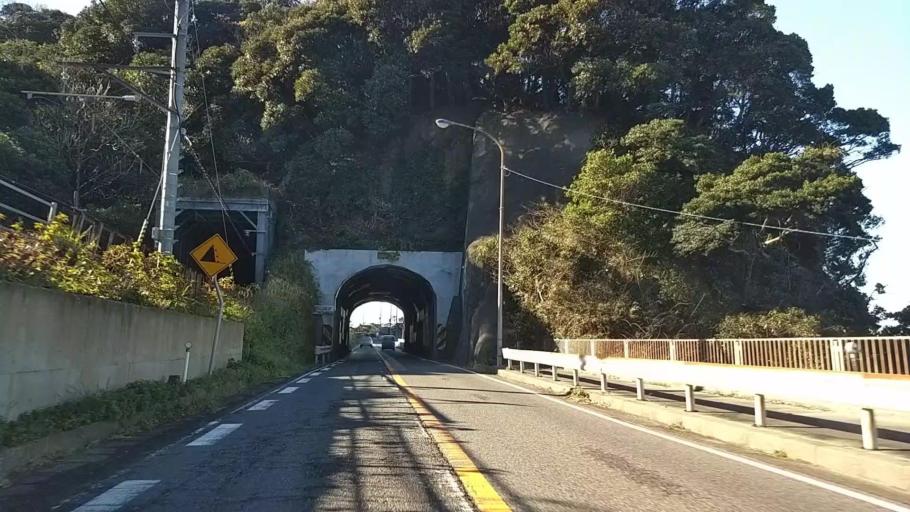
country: JP
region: Chiba
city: Futtsu
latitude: 35.1923
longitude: 139.8222
